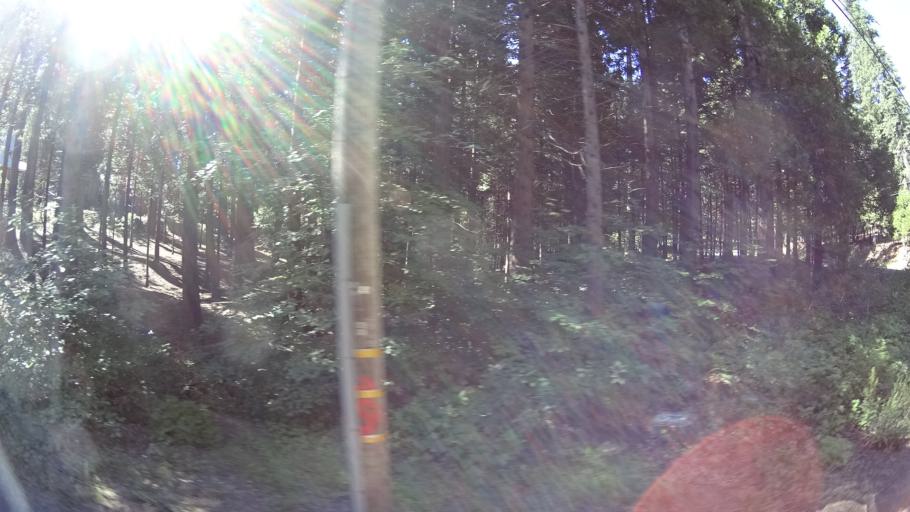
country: US
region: California
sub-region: Calaveras County
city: Arnold
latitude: 38.2898
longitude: -120.2753
